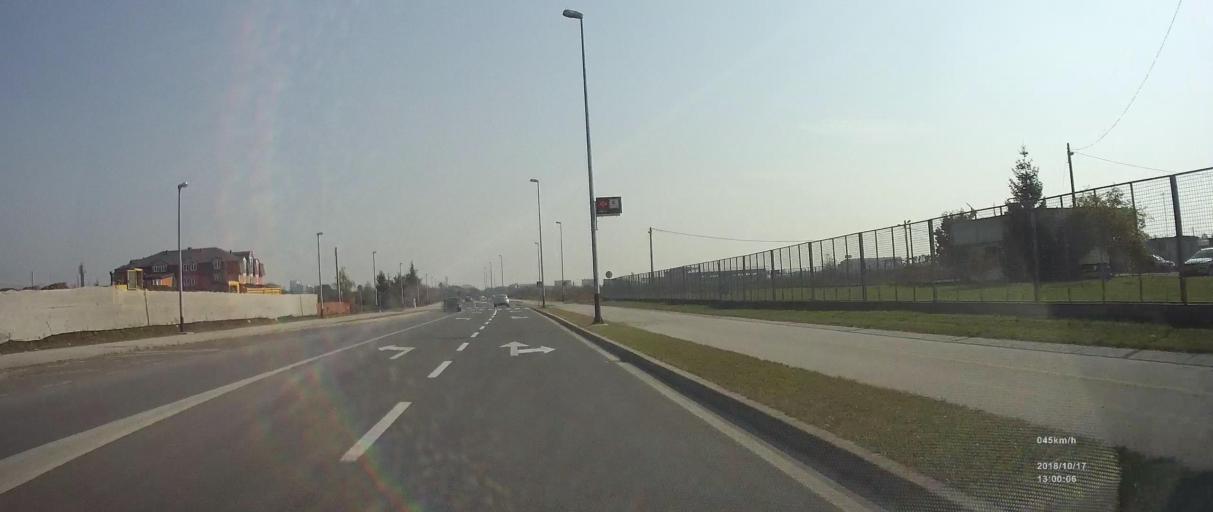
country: HR
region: Zagrebacka
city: Gradici
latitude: 45.7163
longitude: 16.0505
